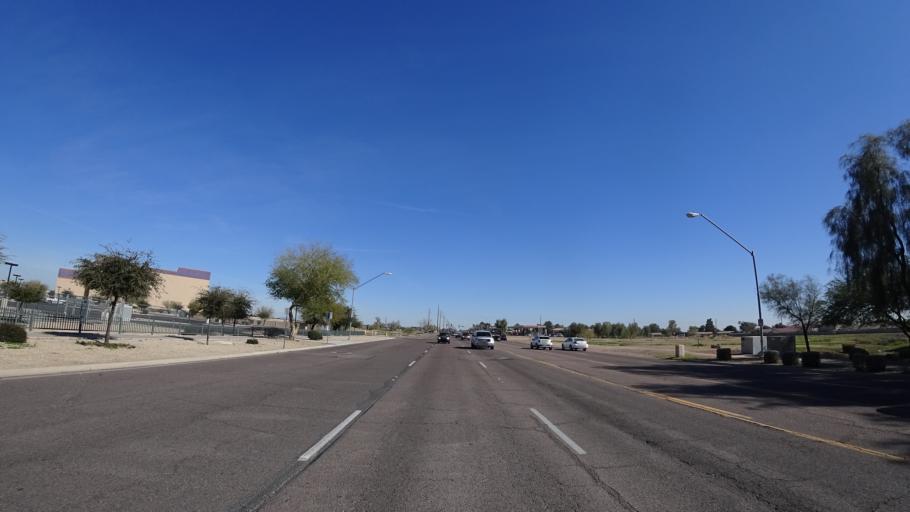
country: US
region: Arizona
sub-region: Maricopa County
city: Tolleson
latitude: 33.5088
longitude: -112.2582
